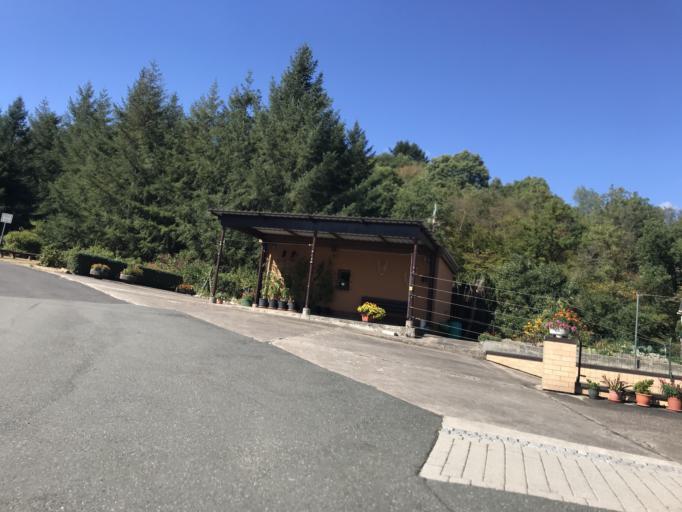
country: DE
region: Hesse
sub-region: Regierungsbezirk Darmstadt
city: Bad Schwalbach
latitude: 50.0901
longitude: 8.0112
